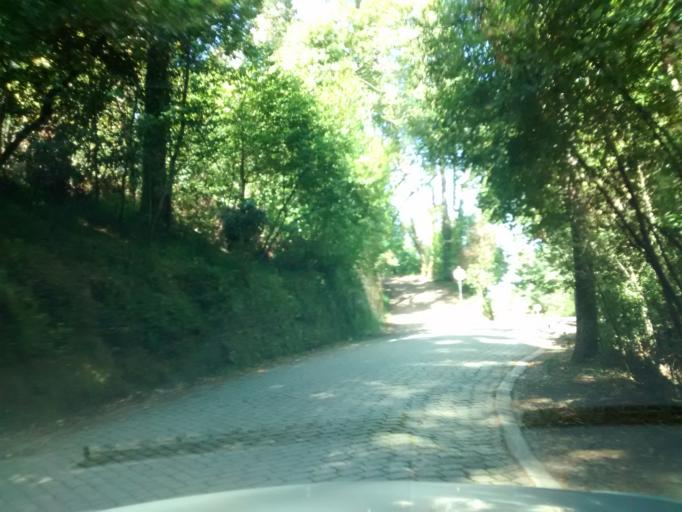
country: PT
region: Aveiro
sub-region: Mealhada
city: Pampilhosa do Botao
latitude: 40.3760
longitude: -8.3631
